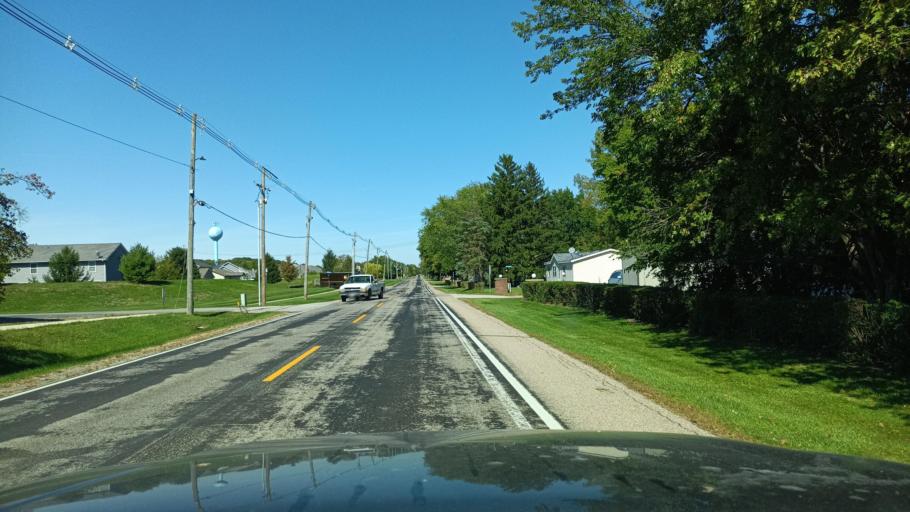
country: US
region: Illinois
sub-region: Champaign County
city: Lake of the Woods
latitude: 40.1999
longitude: -88.3653
